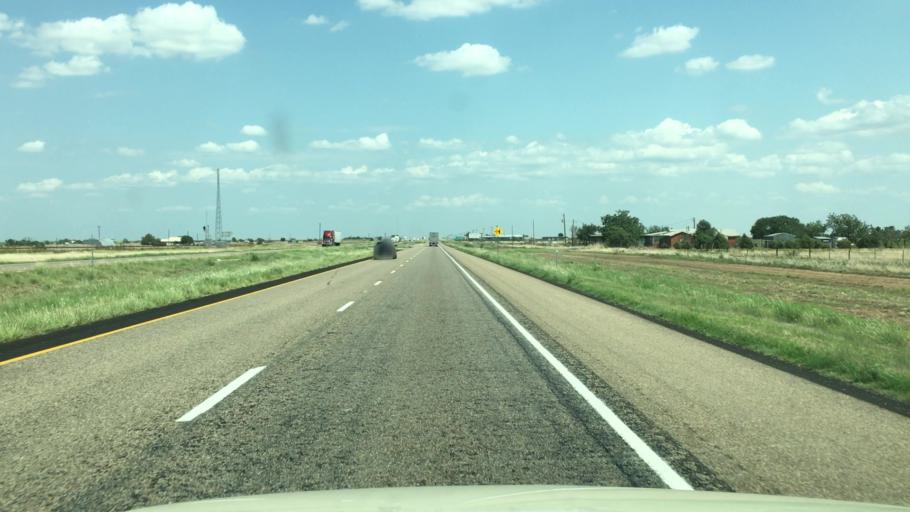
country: US
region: Texas
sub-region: Armstrong County
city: Claude
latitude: 35.0342
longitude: -101.1914
